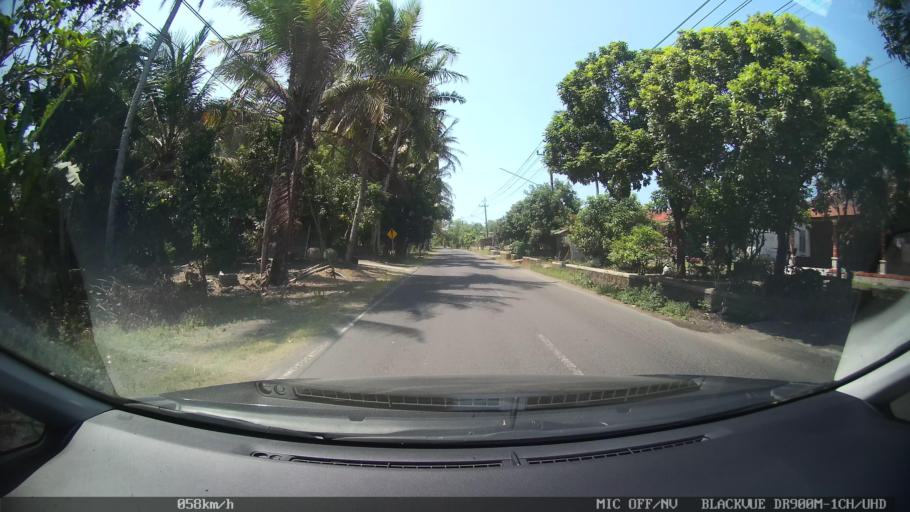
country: ID
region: Daerah Istimewa Yogyakarta
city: Srandakan
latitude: -7.9172
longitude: 110.1049
